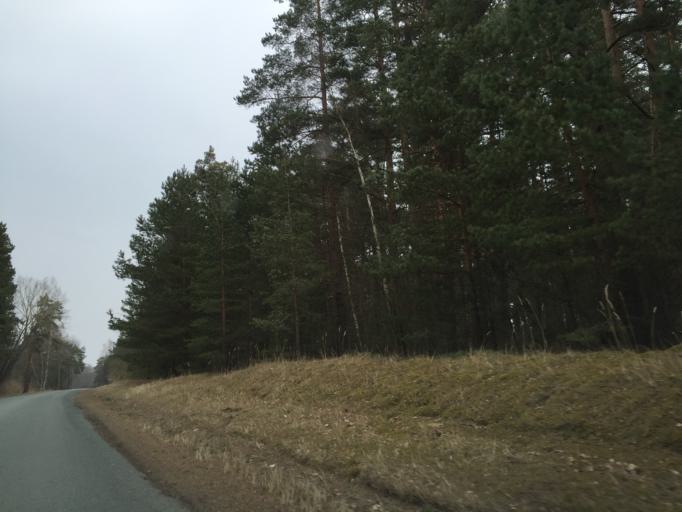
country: LV
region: Salacgrivas
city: Ainazi
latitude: 57.9946
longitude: 24.4294
